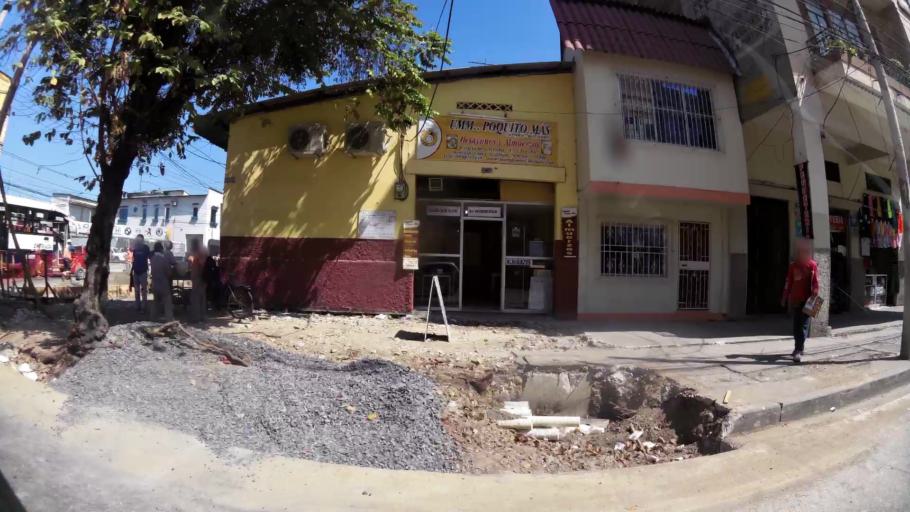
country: EC
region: Guayas
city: Guayaquil
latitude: -2.1910
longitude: -79.8936
